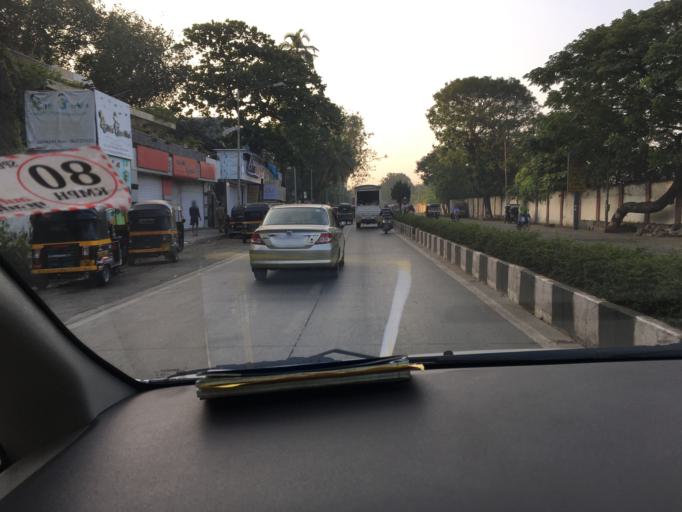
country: IN
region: Maharashtra
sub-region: Mumbai Suburban
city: Mumbai
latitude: 19.0999
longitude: 72.8395
